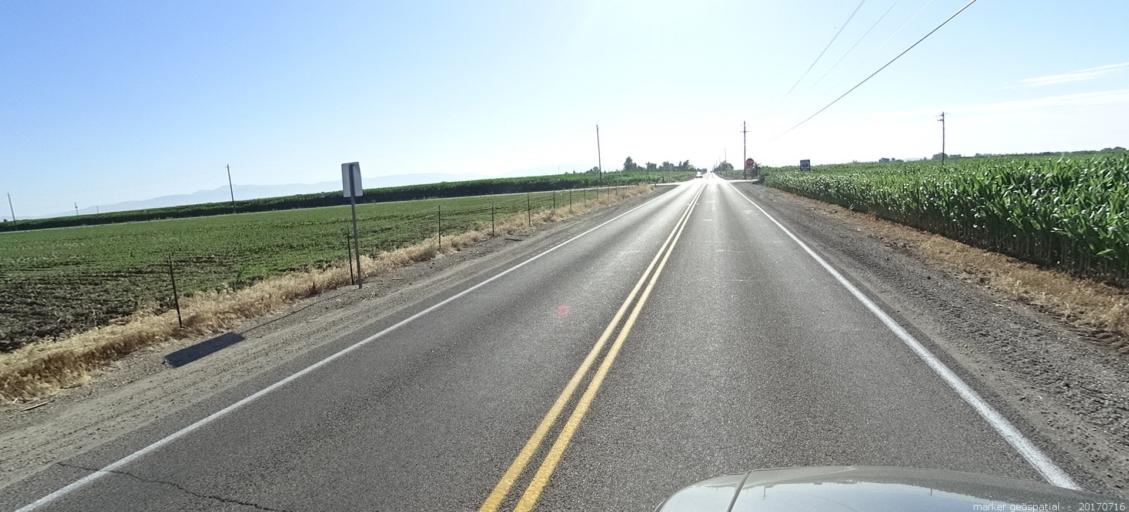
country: US
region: Idaho
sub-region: Ada County
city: Meridian
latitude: 43.5464
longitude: -116.3758
